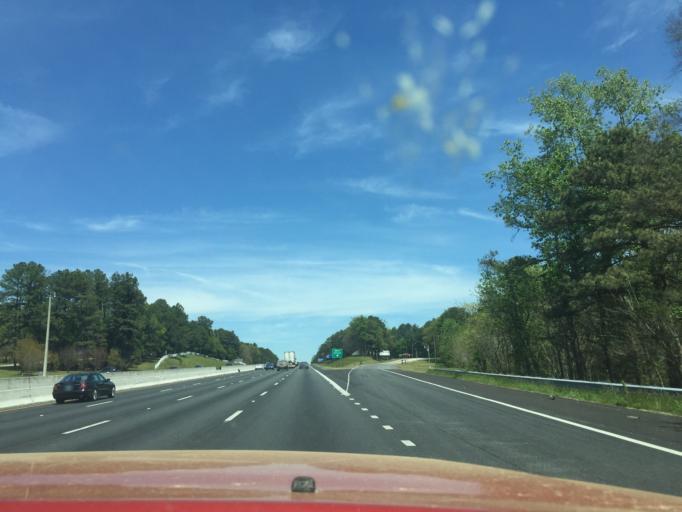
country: US
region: North Carolina
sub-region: Mecklenburg County
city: Pineville
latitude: 35.0771
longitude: -80.9443
